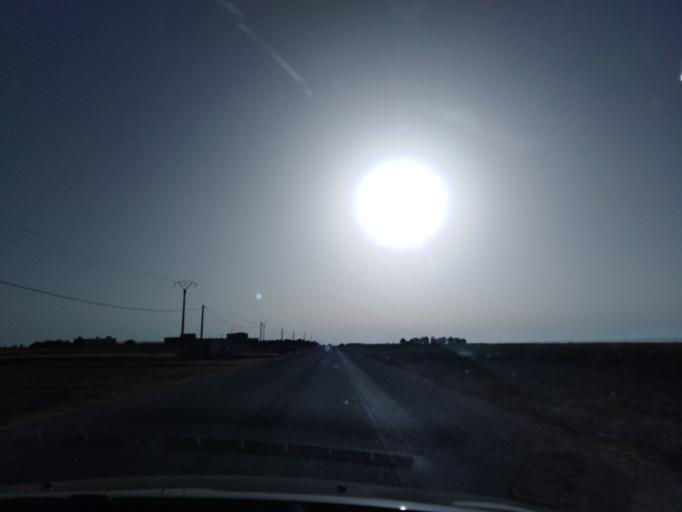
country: MA
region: Doukkala-Abda
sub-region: Safi
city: Safi
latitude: 32.4781
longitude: -8.8923
